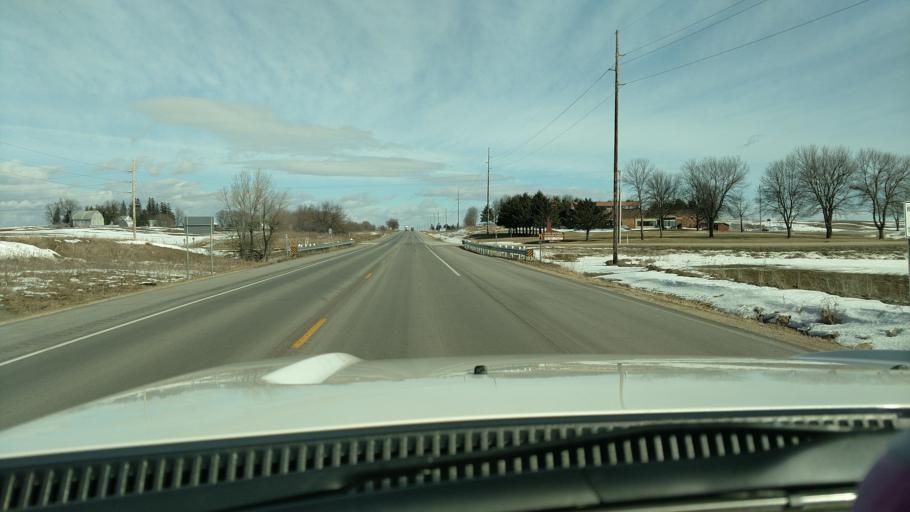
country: US
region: Minnesota
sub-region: Wabasha County
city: Elgin
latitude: 44.1463
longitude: -92.2208
